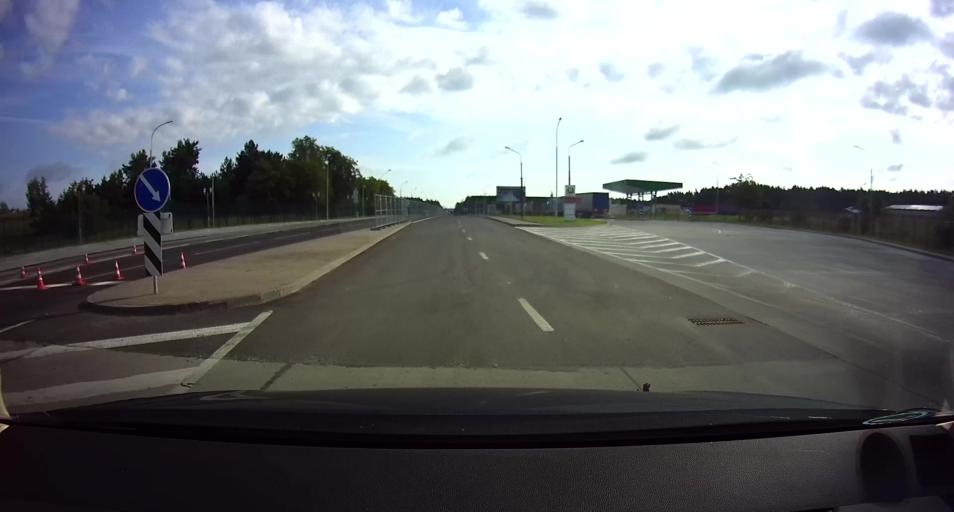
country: PL
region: Podlasie
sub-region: Powiat sokolski
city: Kuznica
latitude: 53.5218
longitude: 23.6603
